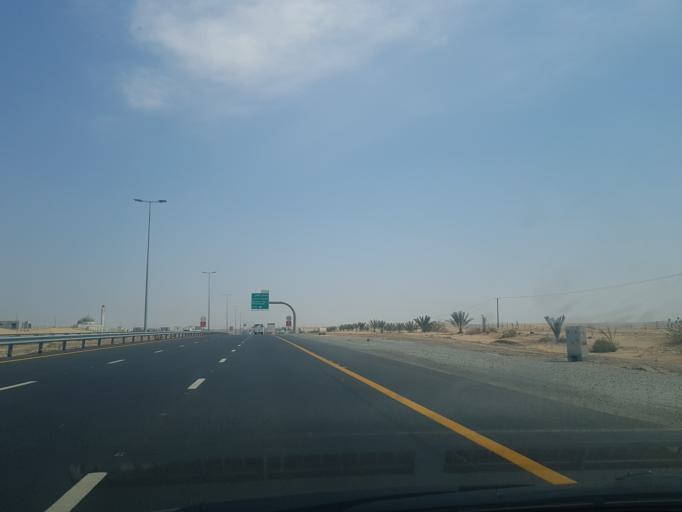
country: AE
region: Ash Shariqah
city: Sharjah
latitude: 25.2288
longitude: 55.5912
